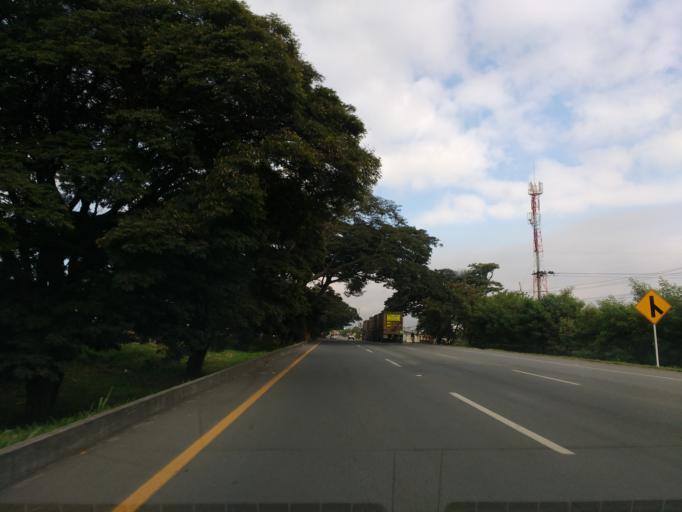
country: CO
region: Valle del Cauca
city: Cali
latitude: 3.4939
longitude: -76.4724
